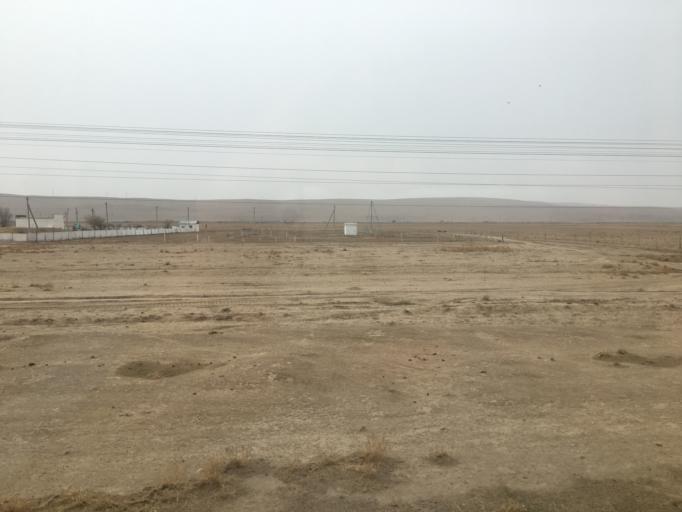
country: TM
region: Mary
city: Serhetabat
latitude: 35.6110
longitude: 62.5395
